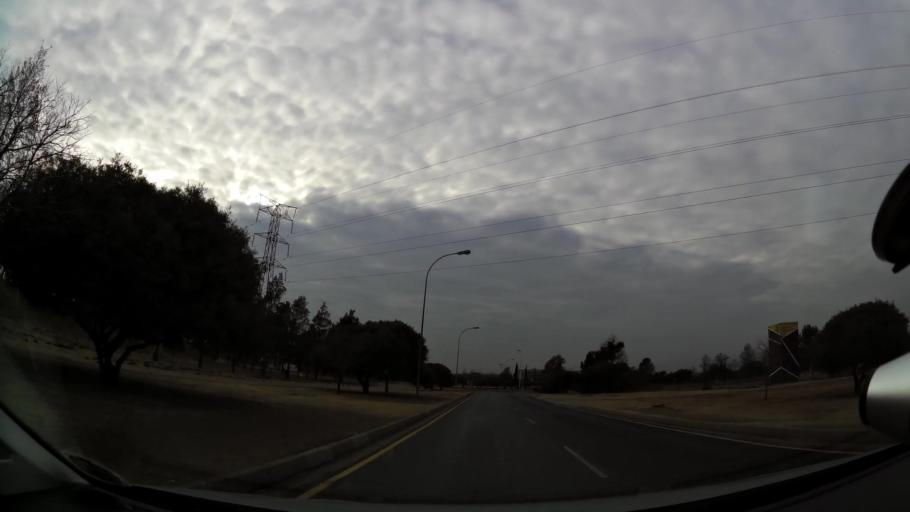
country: ZA
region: Orange Free State
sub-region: Mangaung Metropolitan Municipality
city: Bloemfontein
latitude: -29.1096
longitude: 26.1770
